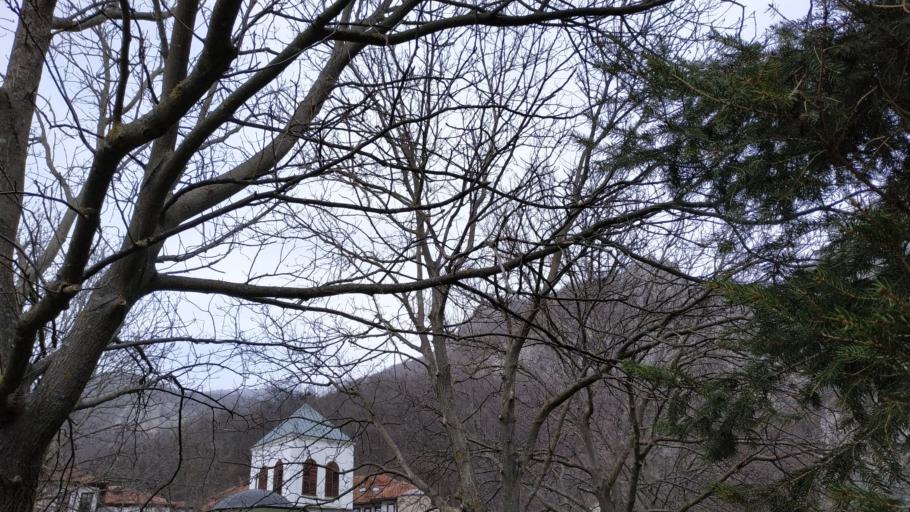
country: RS
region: Central Serbia
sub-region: Zajecarski Okrug
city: Soko Banja
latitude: 43.5611
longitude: 21.8345
